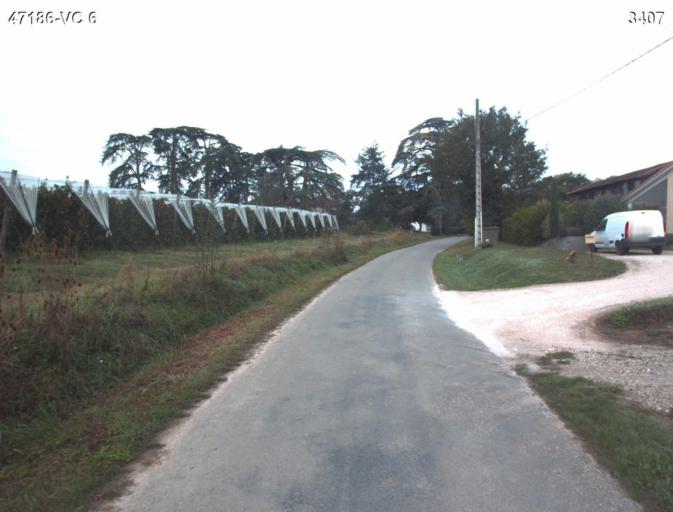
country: FR
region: Aquitaine
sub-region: Departement du Lot-et-Garonne
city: Sainte-Colombe-en-Bruilhois
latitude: 44.2162
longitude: 0.4736
